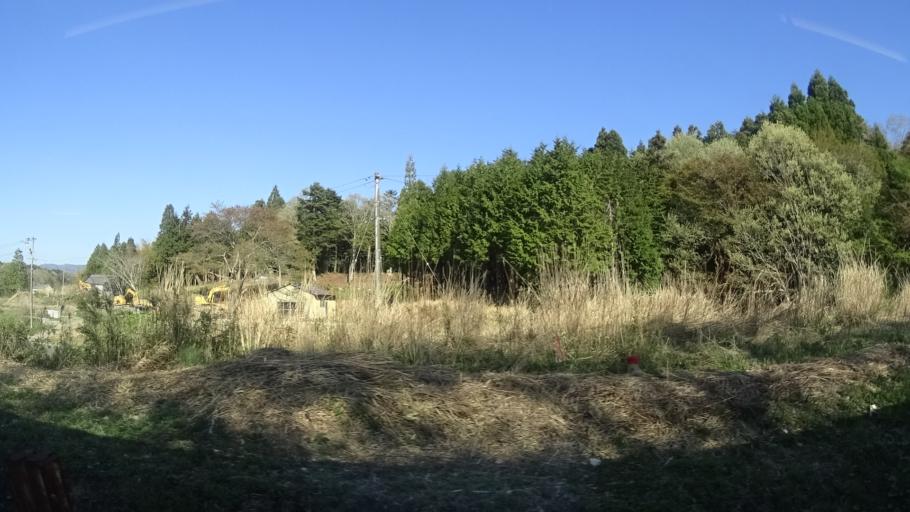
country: JP
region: Fukushima
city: Namie
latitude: 37.5832
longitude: 141.0005
